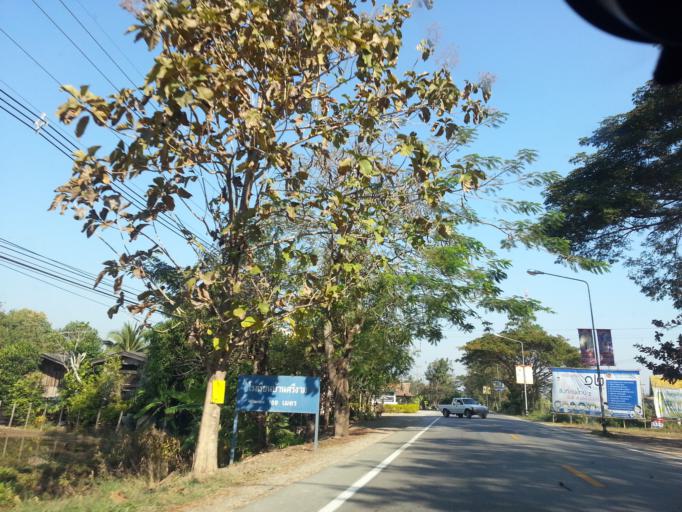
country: TH
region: Chiang Mai
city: Mae Taeng
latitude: 19.0268
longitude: 98.9678
